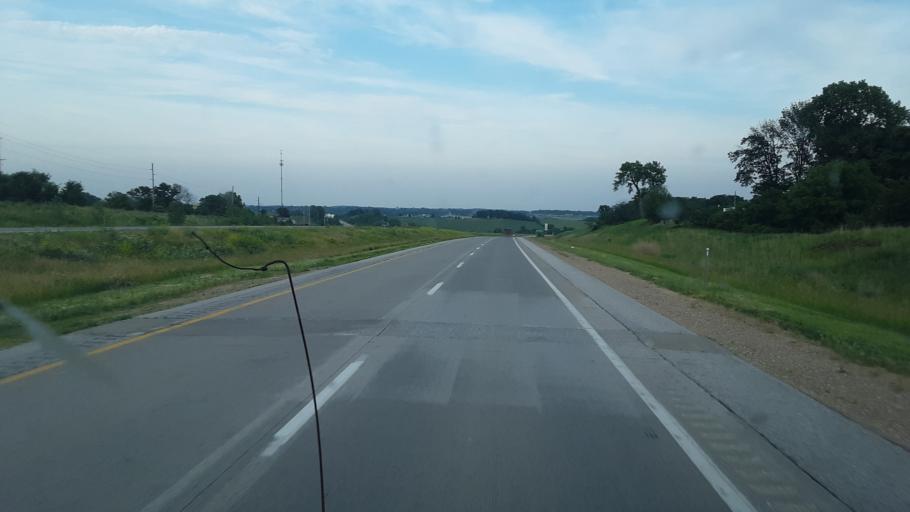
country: US
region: Iowa
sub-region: Tama County
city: Toledo
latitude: 41.9937
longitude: -92.6220
